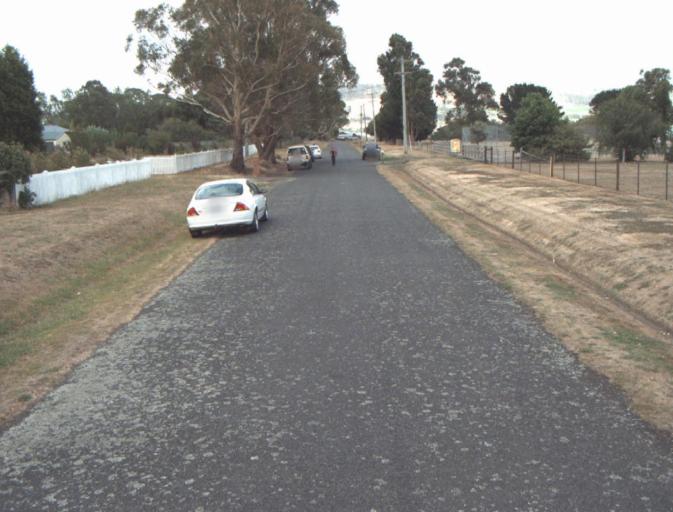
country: AU
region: Tasmania
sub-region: Launceston
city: Mayfield
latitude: -41.3311
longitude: 147.0562
